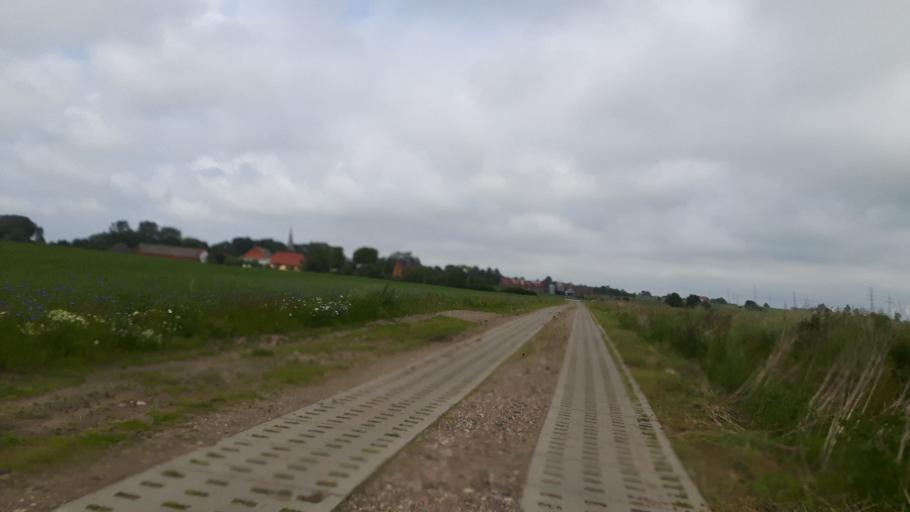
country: PL
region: West Pomeranian Voivodeship
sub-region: Powiat koszalinski
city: Sianow
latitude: 54.2908
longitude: 16.2697
